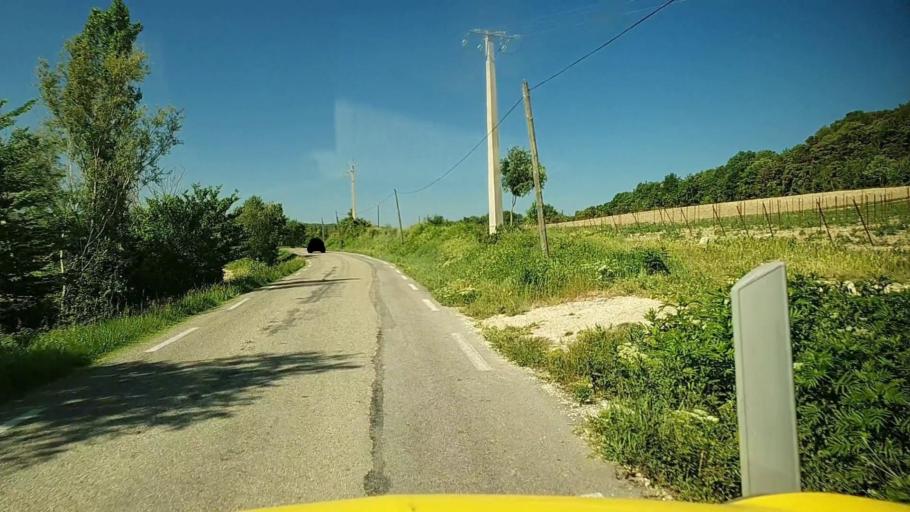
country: FR
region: Languedoc-Roussillon
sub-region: Departement du Gard
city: Blauzac
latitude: 43.9479
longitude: 4.3753
